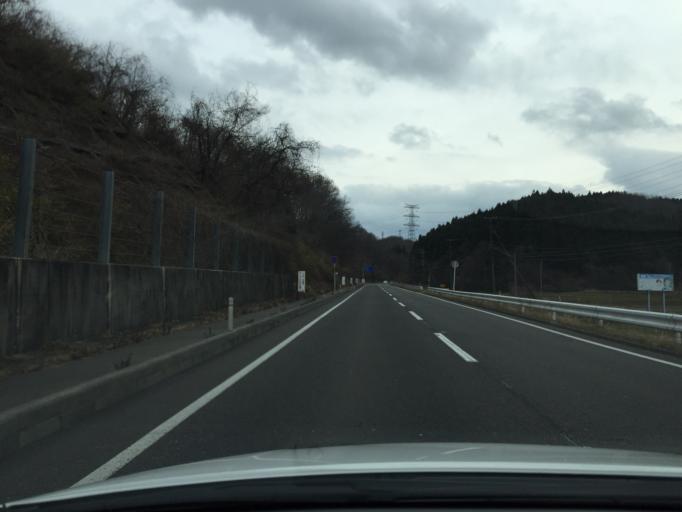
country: JP
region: Fukushima
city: Ishikawa
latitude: 37.1851
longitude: 140.6462
